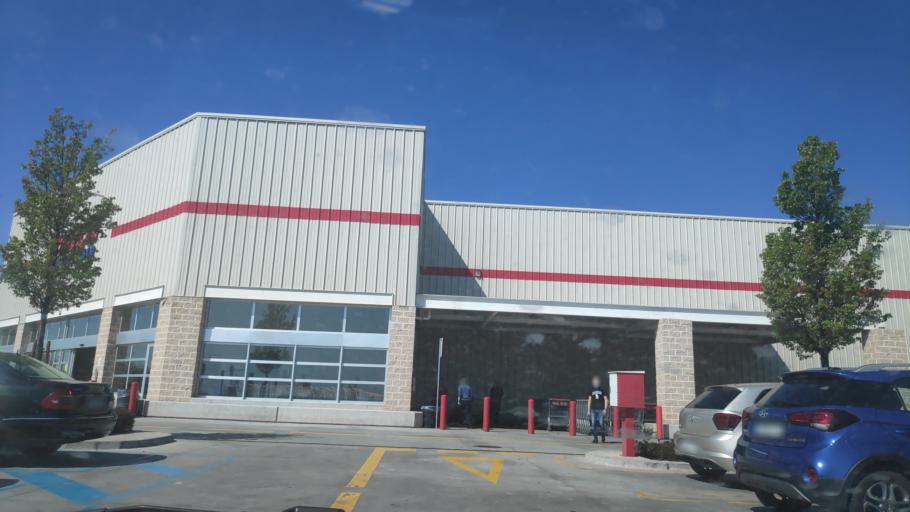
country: ES
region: Madrid
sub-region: Provincia de Madrid
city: Pinto
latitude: 40.2828
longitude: -3.6881
